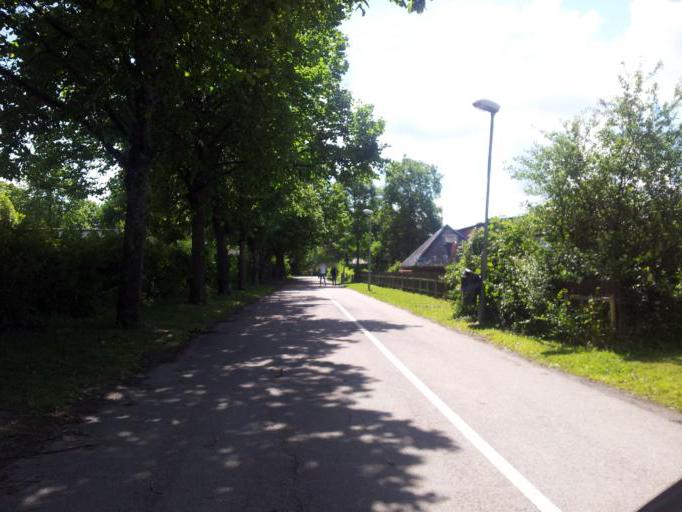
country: SE
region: Uppsala
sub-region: Uppsala Kommun
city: Uppsala
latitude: 59.8693
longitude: 17.6523
